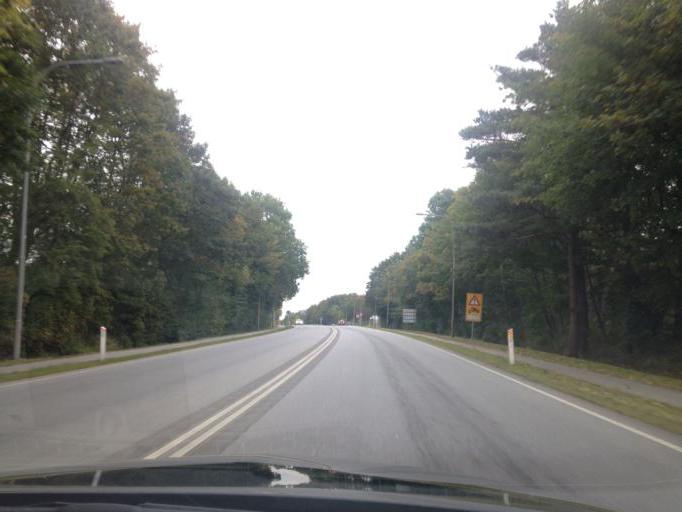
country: DK
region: South Denmark
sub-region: Haderslev Kommune
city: Haderslev
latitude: 55.2653
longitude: 9.4910
